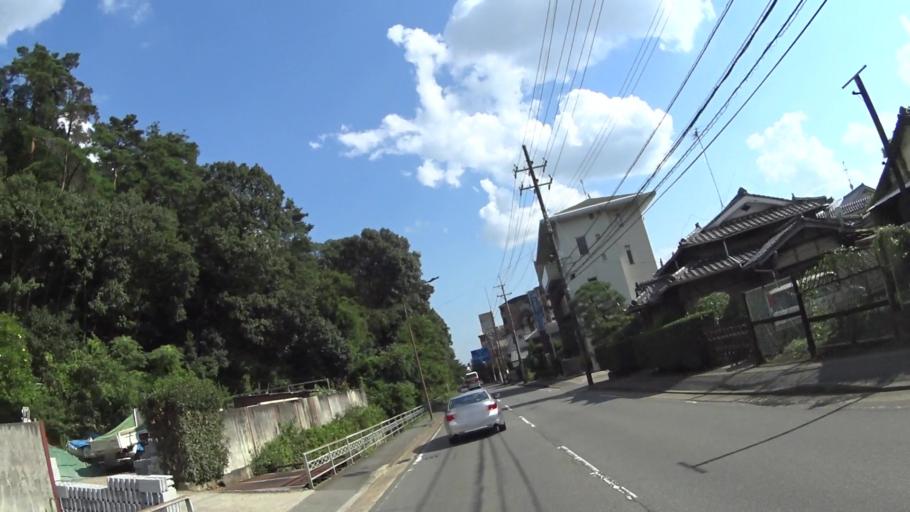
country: JP
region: Kyoto
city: Kyoto
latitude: 35.0220
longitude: 135.7120
